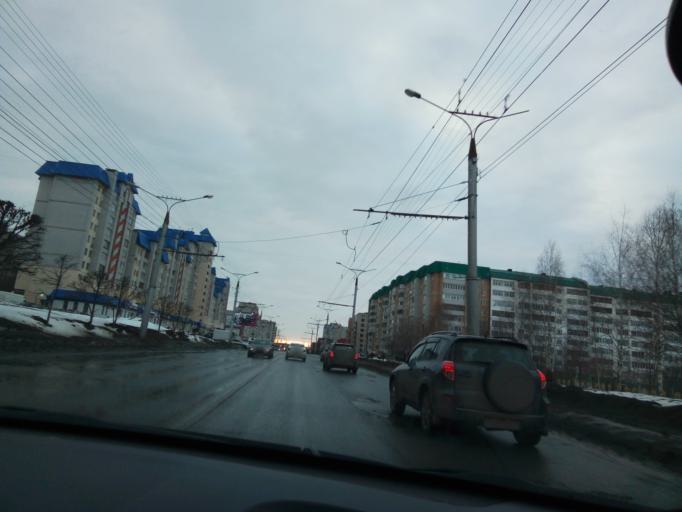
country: RU
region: Chuvashia
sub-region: Cheboksarskiy Rayon
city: Cheboksary
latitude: 56.1488
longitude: 47.1832
